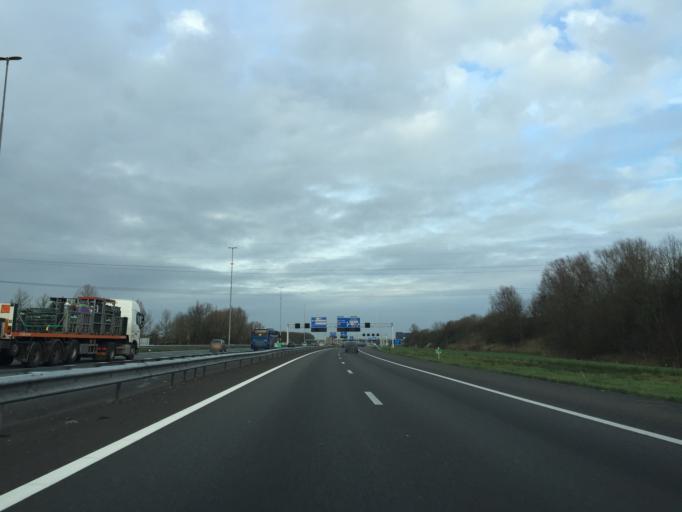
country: NL
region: Utrecht
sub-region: Gemeente Nieuwegein
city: Nieuwegein
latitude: 52.0534
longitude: 5.0654
